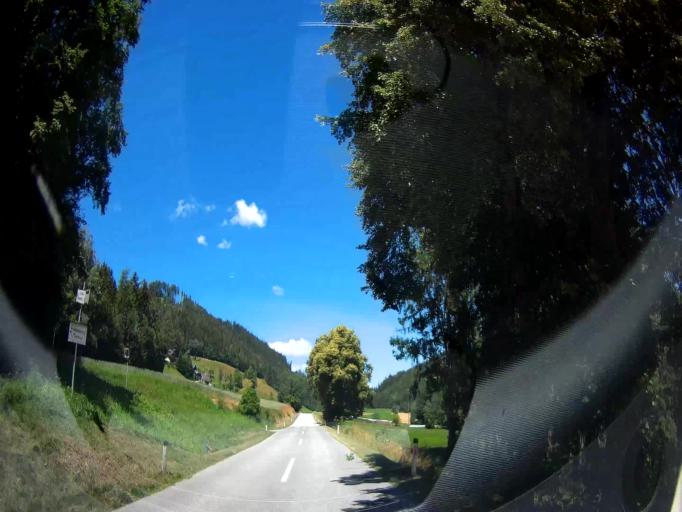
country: AT
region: Carinthia
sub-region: Politischer Bezirk Sankt Veit an der Glan
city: St. Georgen am Laengsee
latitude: 46.7173
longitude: 14.4159
